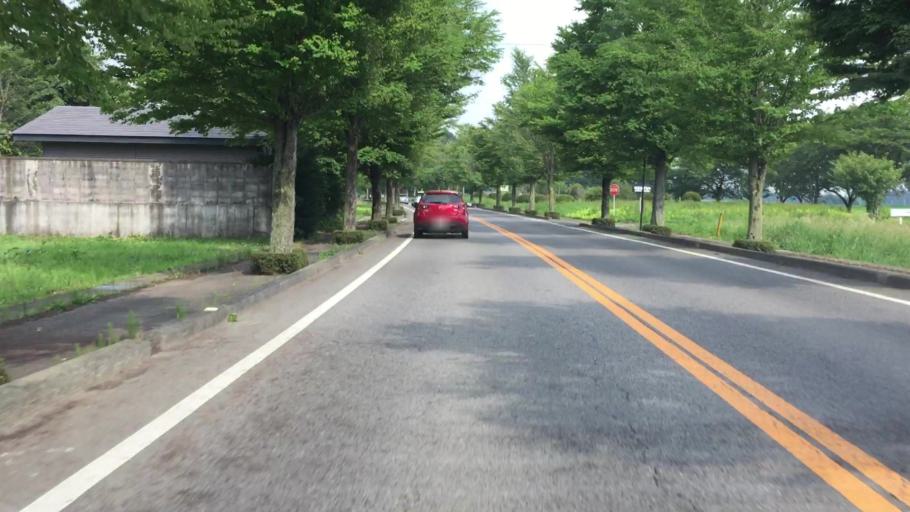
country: JP
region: Tochigi
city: Kuroiso
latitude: 36.9902
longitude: 139.9446
